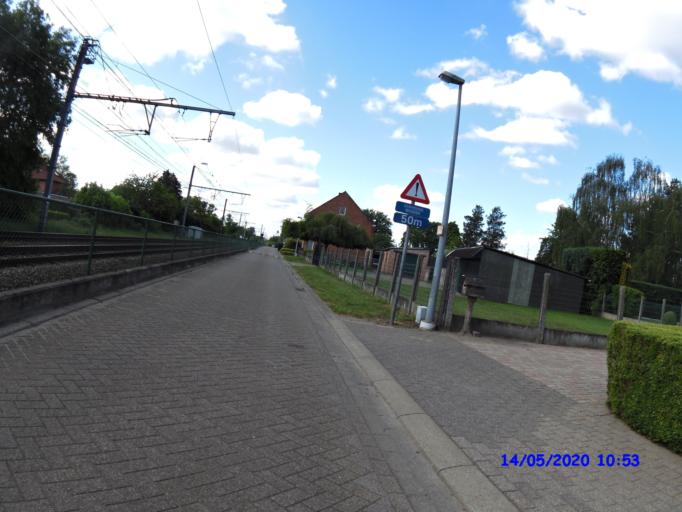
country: BE
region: Flanders
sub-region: Provincie Antwerpen
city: Vosselaar
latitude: 51.2401
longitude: 4.8924
